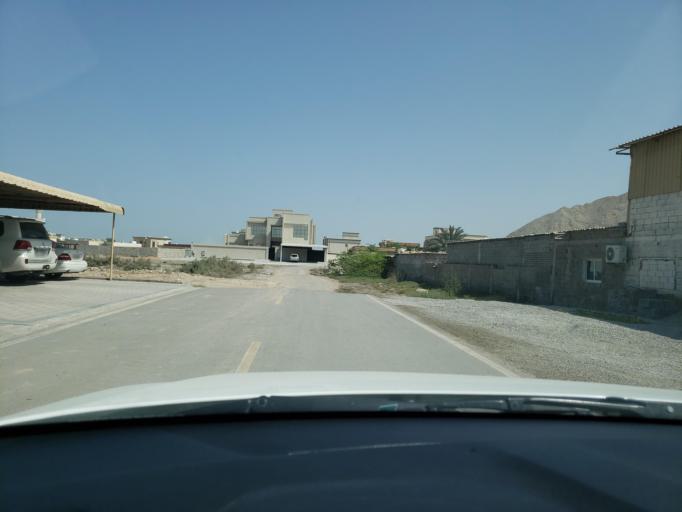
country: AE
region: Ra's al Khaymah
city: Ras al-Khaimah
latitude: 25.8557
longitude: 56.0178
